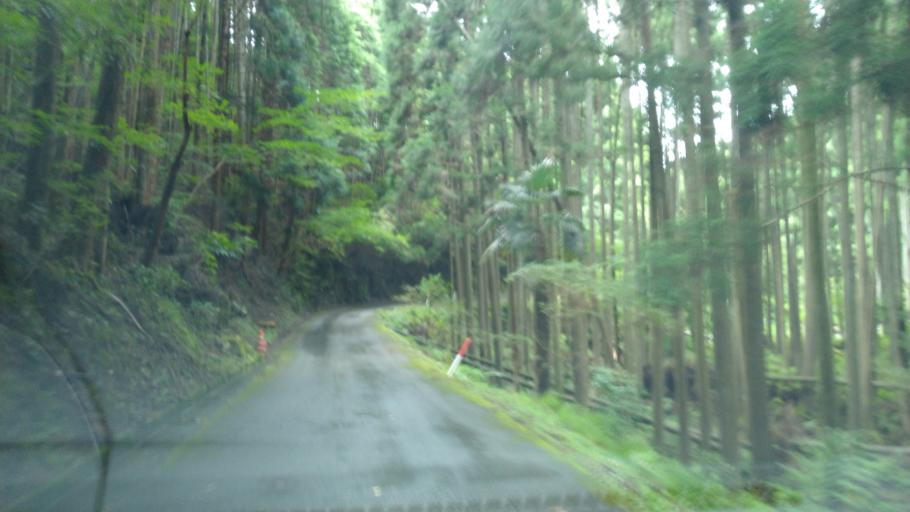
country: JP
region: Kyoto
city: Ayabe
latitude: 35.2344
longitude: 135.2675
